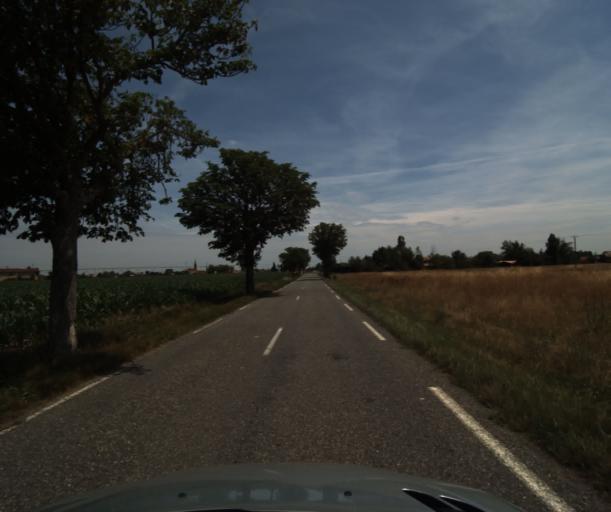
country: FR
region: Midi-Pyrenees
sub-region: Departement de la Haute-Garonne
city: Labastidette
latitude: 43.4542
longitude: 1.2395
